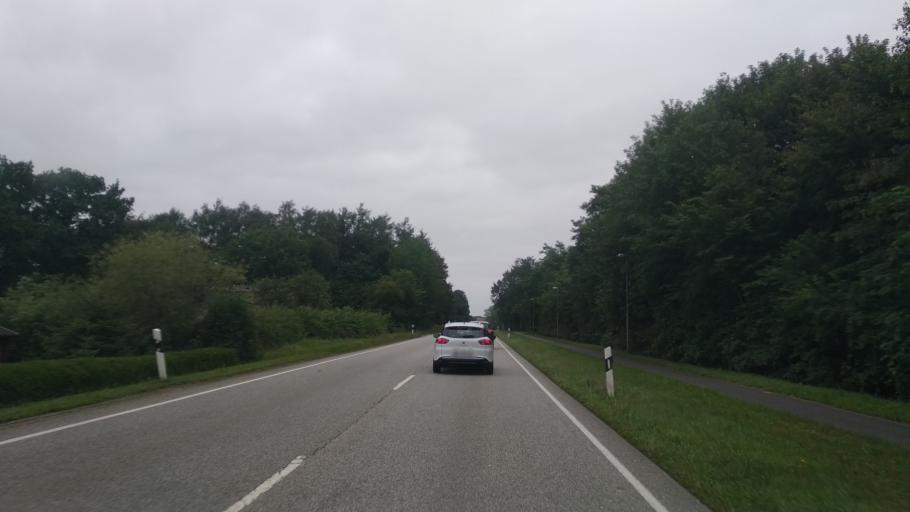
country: DE
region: Schleswig-Holstein
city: Oeversee
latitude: 54.6973
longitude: 9.4339
